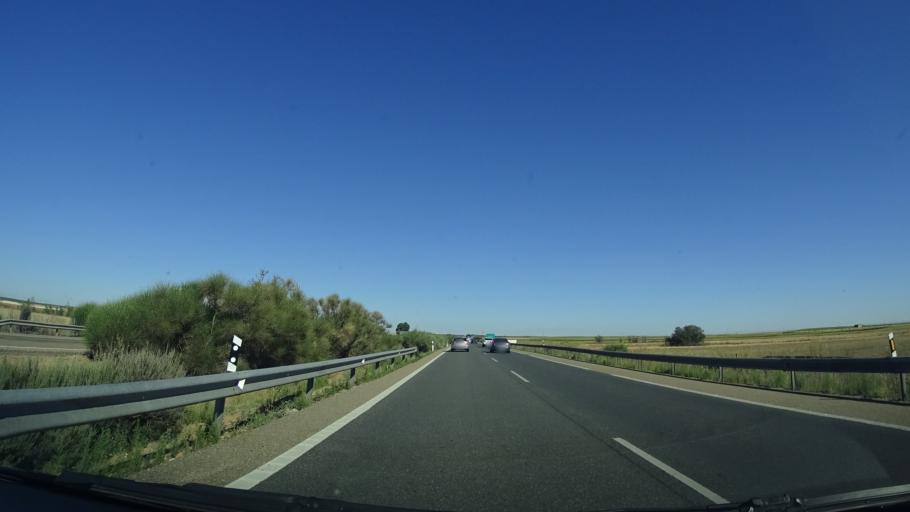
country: ES
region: Castille and Leon
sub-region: Provincia de Valladolid
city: San Pedro de Latarce
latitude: 41.7871
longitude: -5.3272
